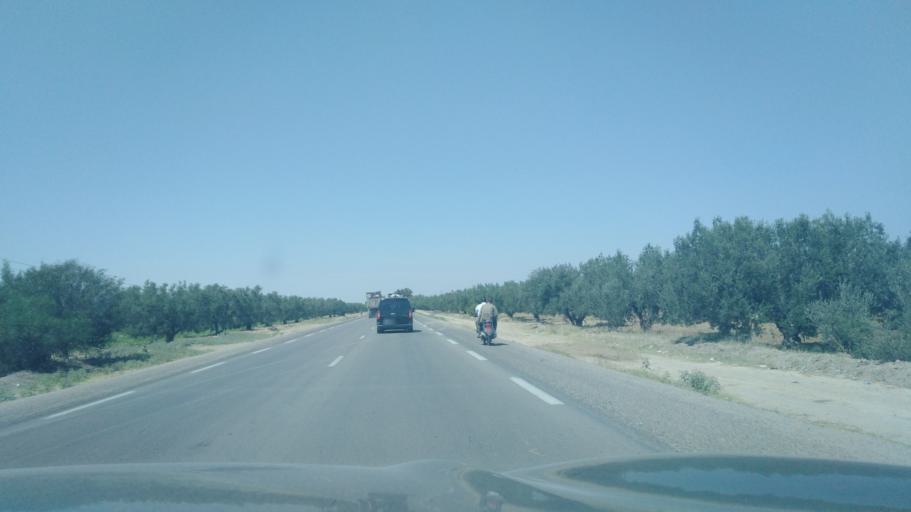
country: TN
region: Al Qayrawan
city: Kairouan
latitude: 35.6111
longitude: 9.9141
